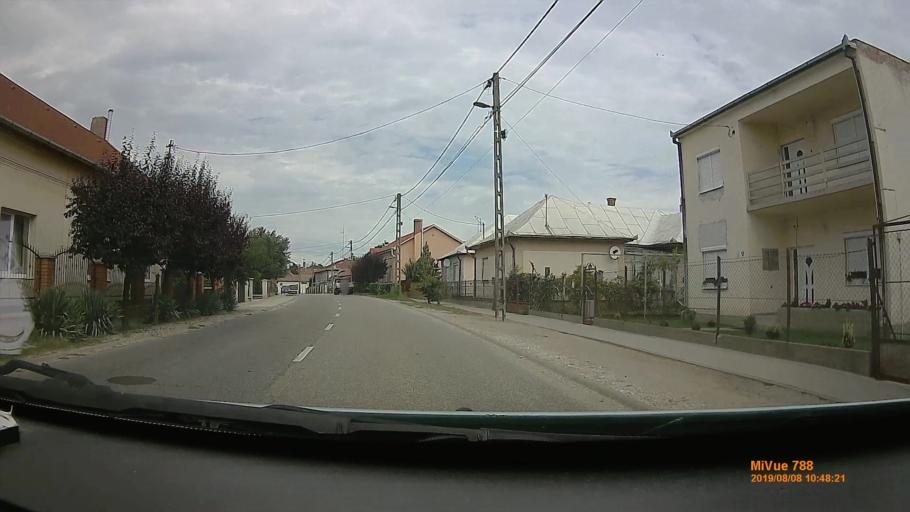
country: HU
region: Szabolcs-Szatmar-Bereg
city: Balkany
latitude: 47.7679
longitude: 21.8634
